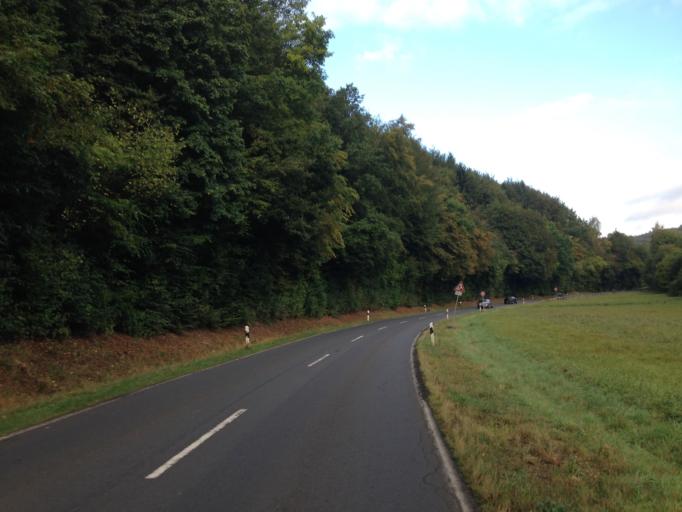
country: DE
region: Hesse
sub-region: Regierungsbezirk Giessen
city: Heuchelheim
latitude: 50.6286
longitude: 8.5753
